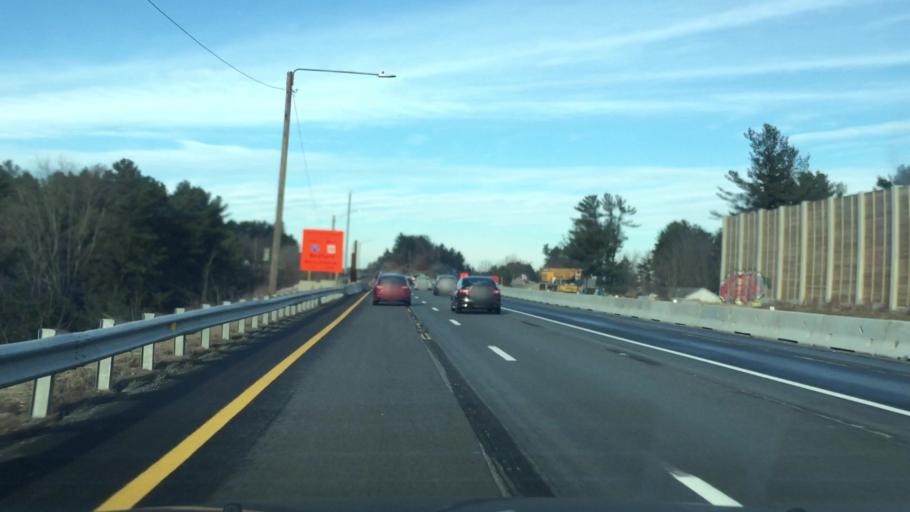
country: US
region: New Hampshire
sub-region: Hillsborough County
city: Manchester
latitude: 42.9524
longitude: -71.4006
